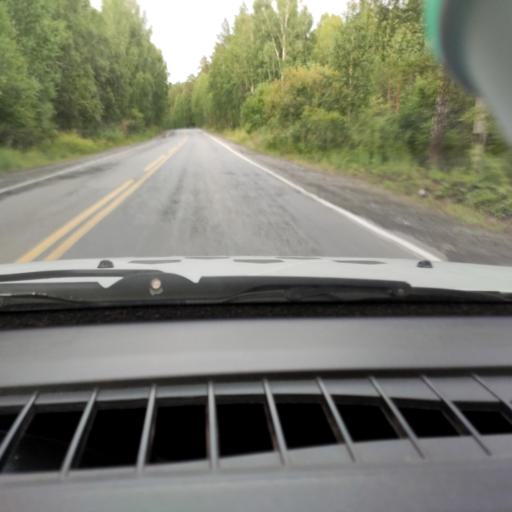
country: RU
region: Chelyabinsk
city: Tayginka
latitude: 55.5588
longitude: 60.3773
